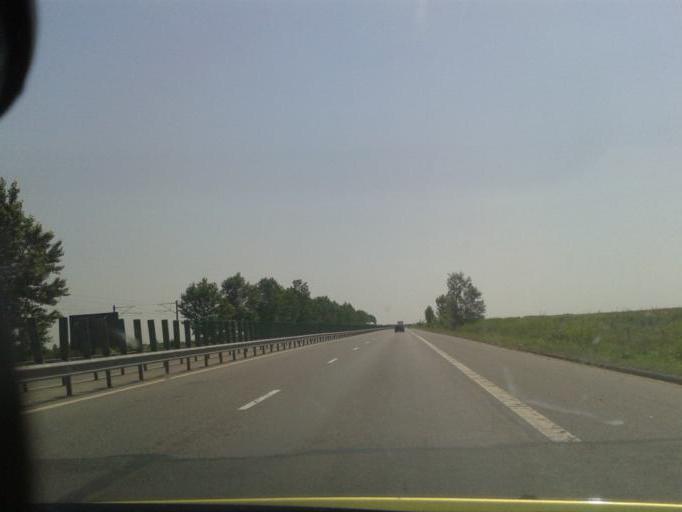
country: RO
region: Calarasi
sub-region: Comuna Tamadau Mare
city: Tamadau Mare
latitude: 44.4461
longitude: 26.5411
